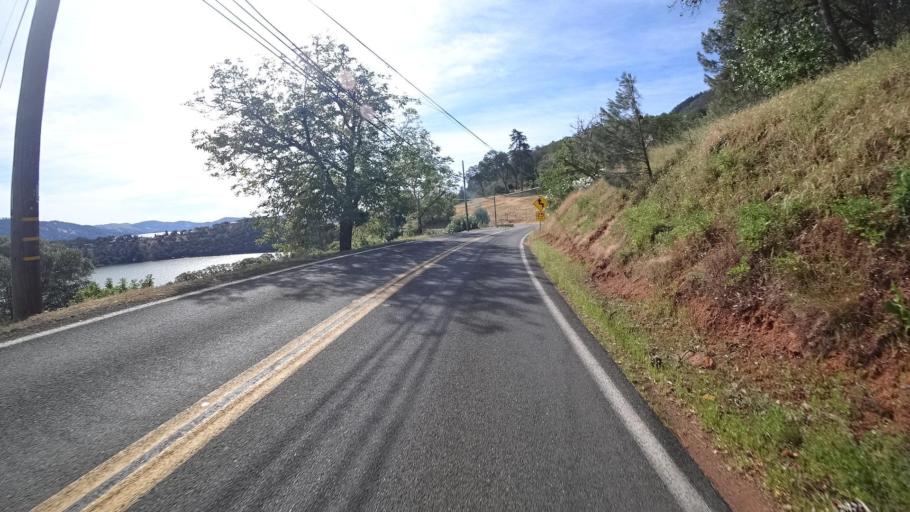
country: US
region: California
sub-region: Lake County
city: Soda Bay
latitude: 39.0087
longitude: -122.7731
